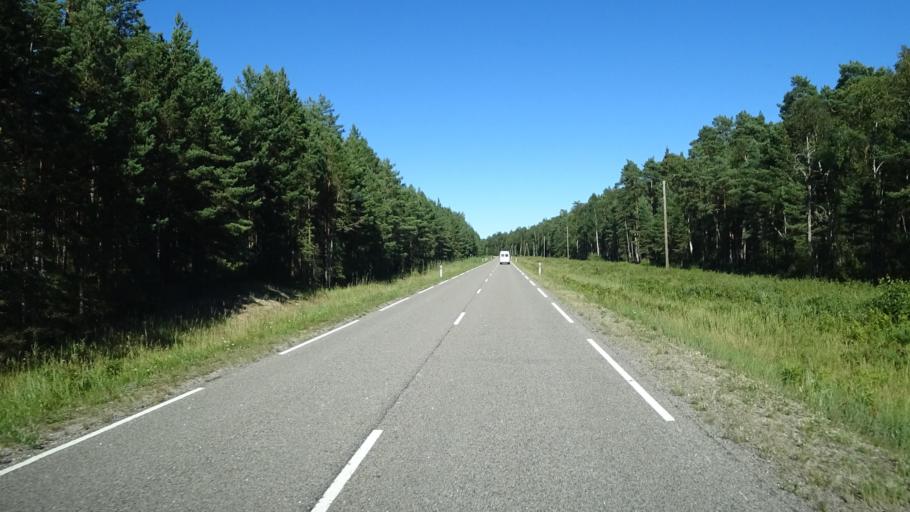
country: LV
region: Dundaga
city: Dundaga
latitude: 57.7194
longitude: 22.4742
